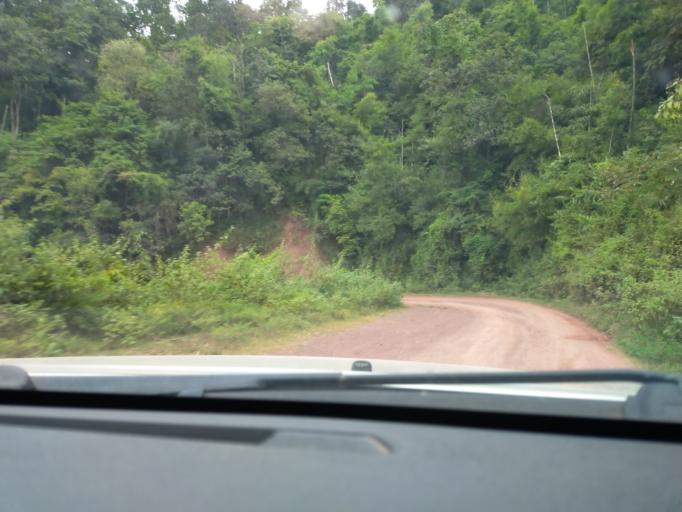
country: TH
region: Nan
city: Chaloem Phra Kiat
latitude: 19.7704
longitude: 101.3494
